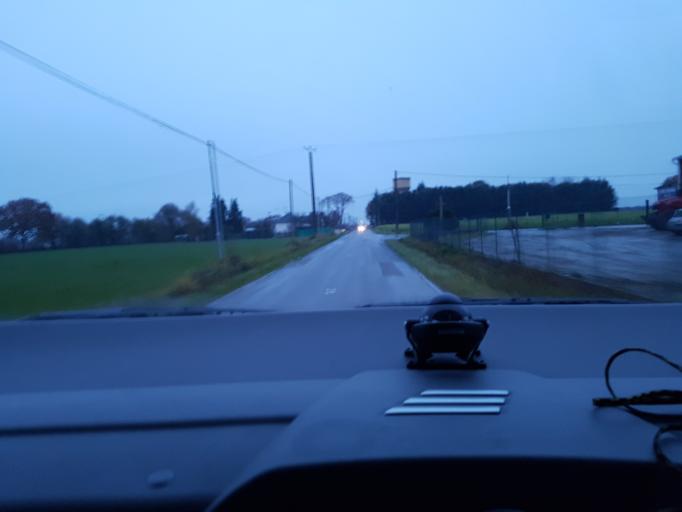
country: FR
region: Brittany
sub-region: Departement d'Ille-et-Vilaine
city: Montreuil-sous-Perouse
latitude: 48.1982
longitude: -1.2683
